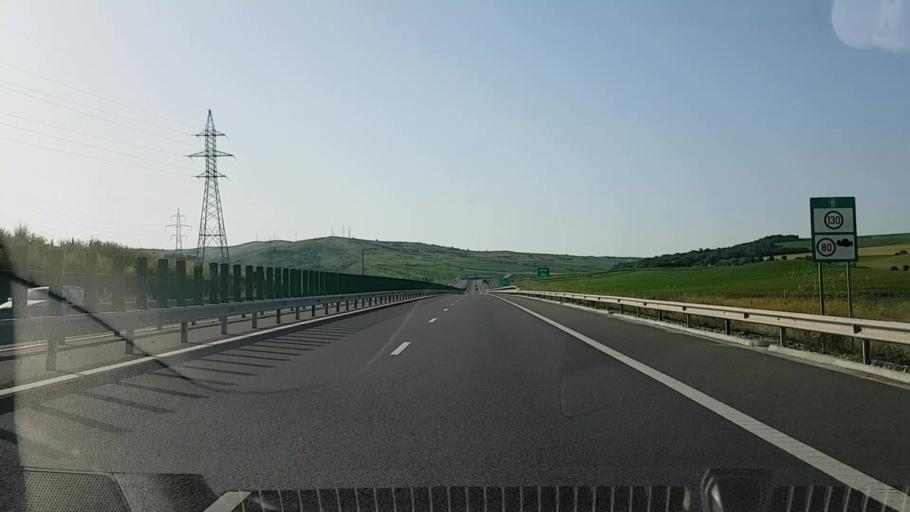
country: RO
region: Alba
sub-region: Comuna Unirea
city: Unirea
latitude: 46.4590
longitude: 23.7858
